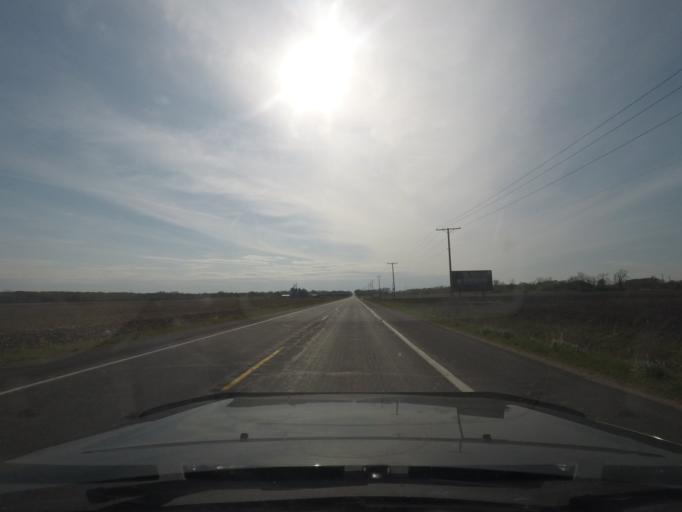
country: US
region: Michigan
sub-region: Berrien County
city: Three Oaks
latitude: 41.7986
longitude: -86.5882
